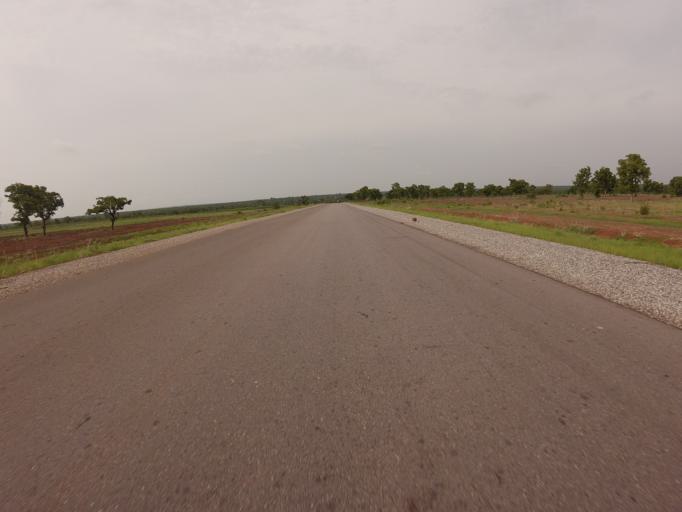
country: GH
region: Northern
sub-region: Yendi
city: Yendi
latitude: 9.8038
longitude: -0.1133
